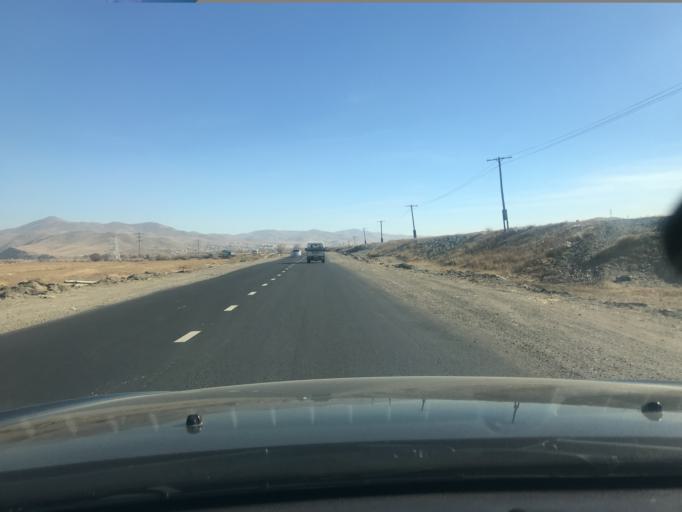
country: MN
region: Ulaanbaatar
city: Ulaanbaatar
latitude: 47.8966
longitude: 107.0480
